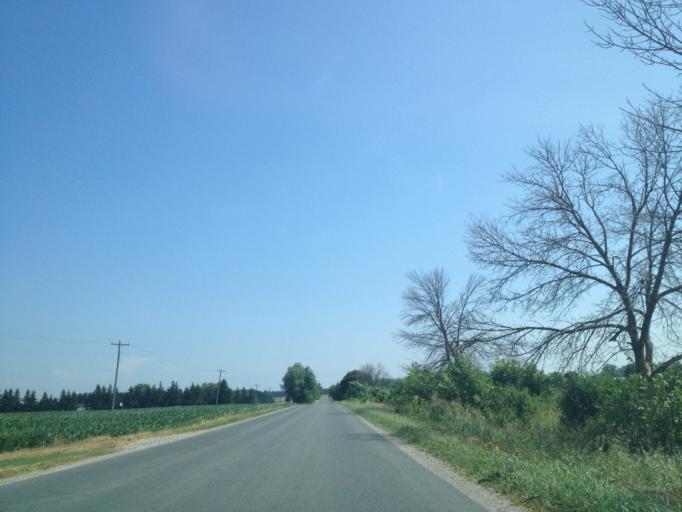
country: CA
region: Ontario
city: Stratford
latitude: 43.2648
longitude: -81.1996
